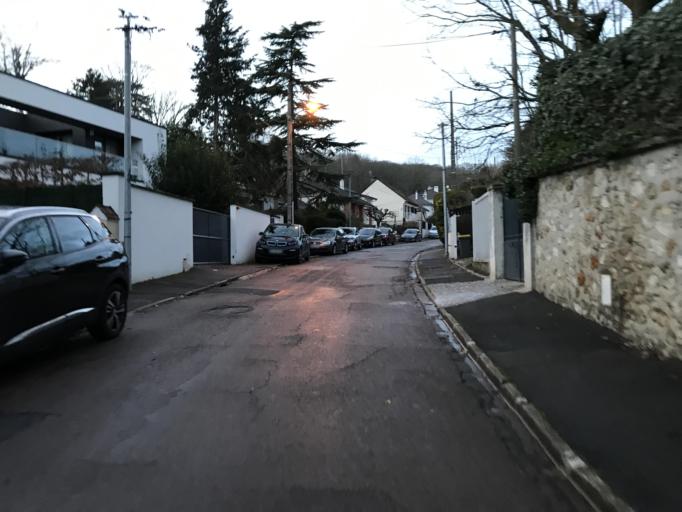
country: FR
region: Ile-de-France
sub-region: Departement de l'Essonne
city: Verrieres-le-Buisson
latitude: 48.7491
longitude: 2.2590
